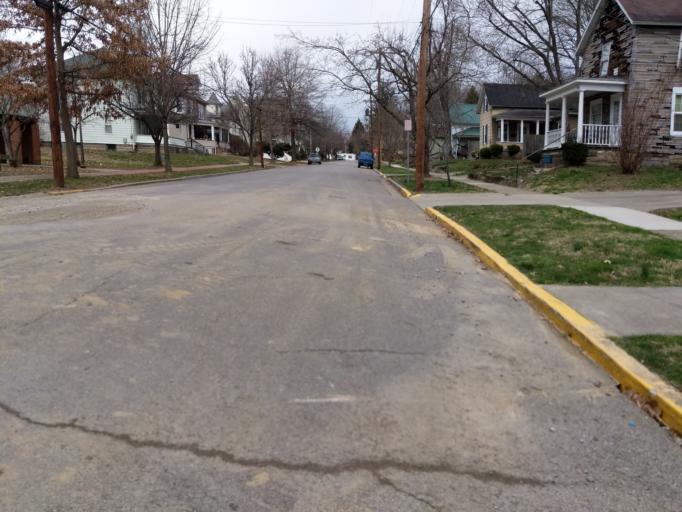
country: US
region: Ohio
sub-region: Athens County
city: Athens
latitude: 39.3346
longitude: -82.1114
